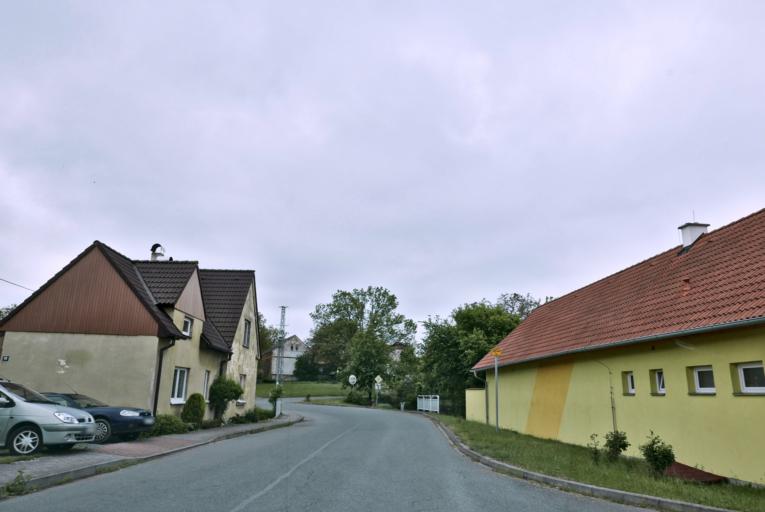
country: CZ
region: Plzensky
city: Kralovice
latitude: 49.9438
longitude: 13.4649
